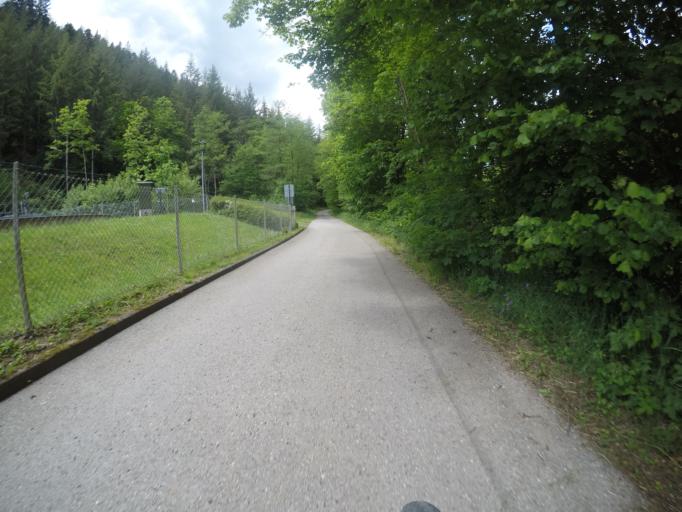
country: DE
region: Baden-Wuerttemberg
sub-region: Karlsruhe Region
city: Wildberg
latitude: 48.6436
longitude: 8.7365
